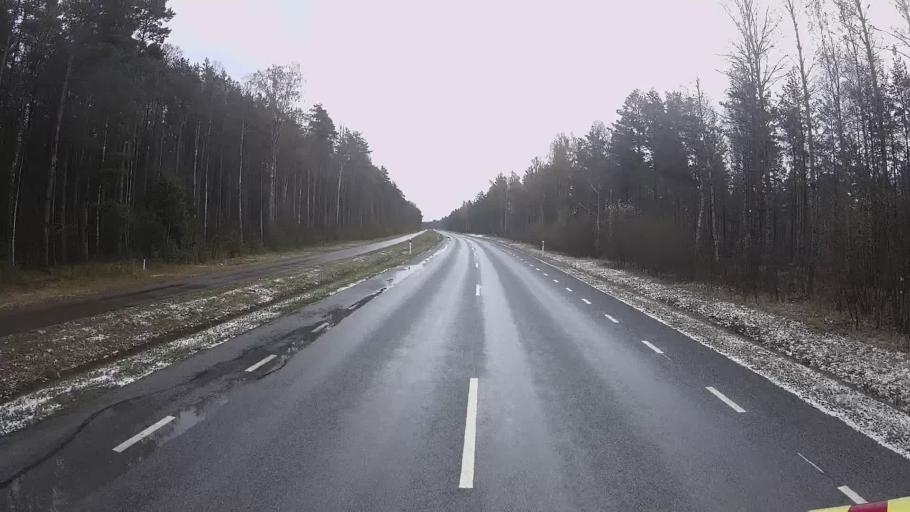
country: EE
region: Hiiumaa
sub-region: Kaerdla linn
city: Kardla
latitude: 59.0040
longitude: 22.6903
